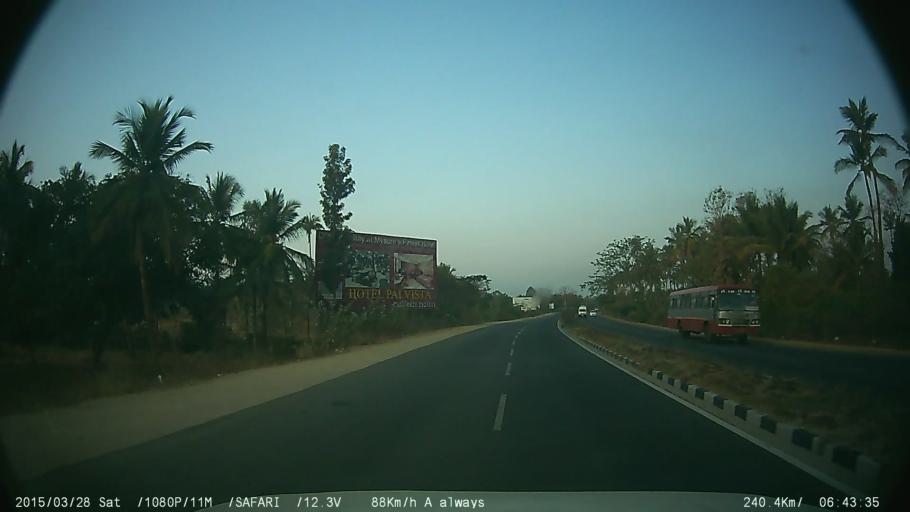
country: IN
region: Karnataka
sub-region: Mandya
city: Maddur
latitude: 12.6316
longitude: 77.1172
